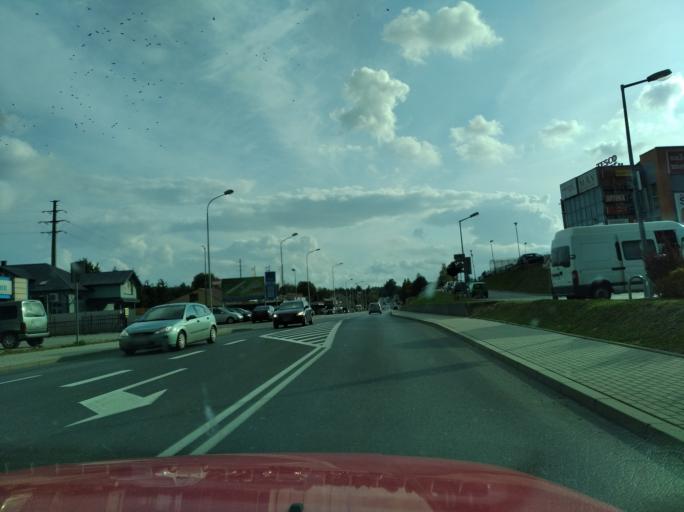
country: PL
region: Subcarpathian Voivodeship
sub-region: Powiat jaroslawski
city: Jaroslaw
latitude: 50.0084
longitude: 22.6764
